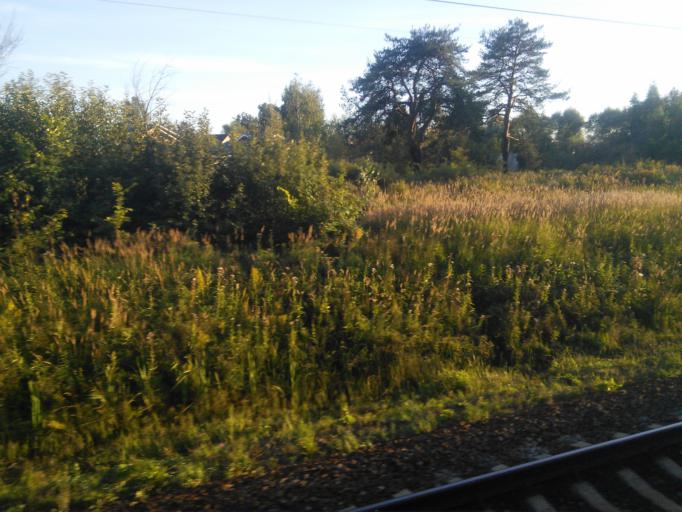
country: RU
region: Moskovskaya
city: Imeni Vorovskogo
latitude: 55.7203
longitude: 38.3835
